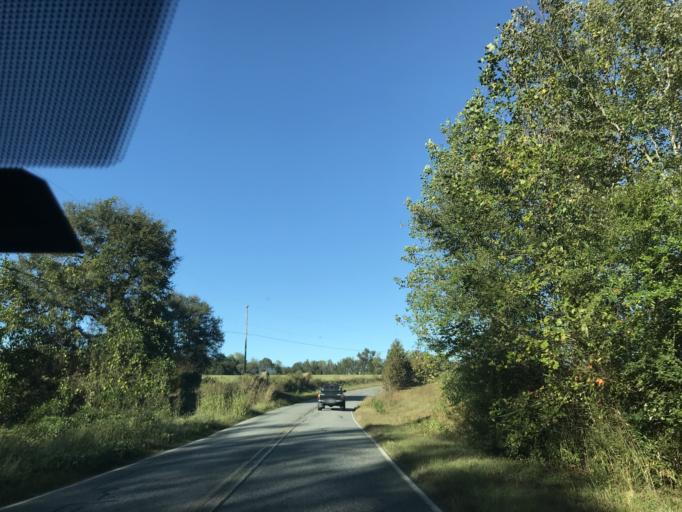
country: US
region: South Carolina
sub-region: Spartanburg County
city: Mayo
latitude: 35.1032
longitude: -81.8468
